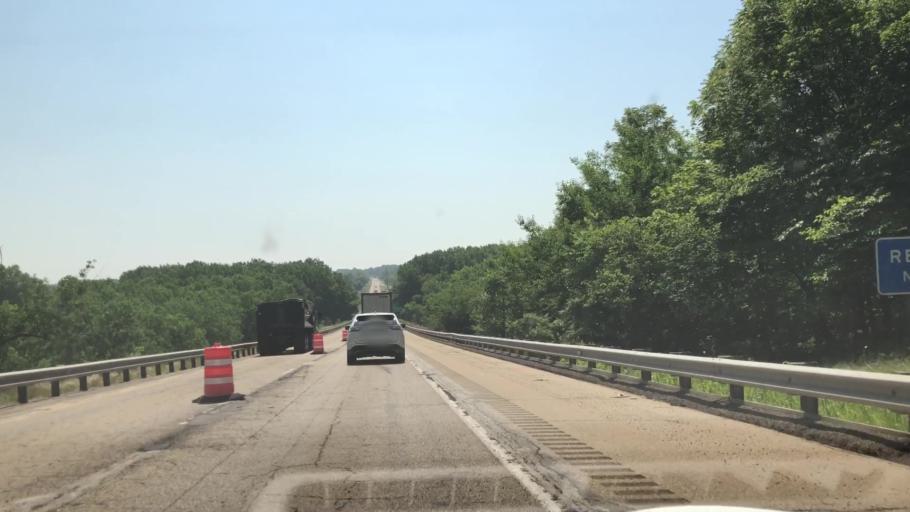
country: US
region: Illinois
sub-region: Woodford County
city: Eureka
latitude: 40.6156
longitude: -89.2557
